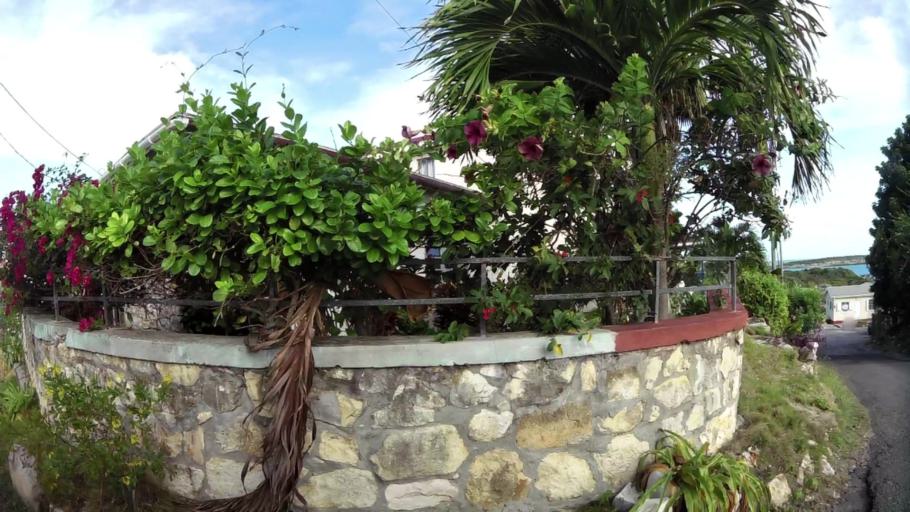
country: AG
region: Saint Peter
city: Parham
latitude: 17.0954
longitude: -61.7236
